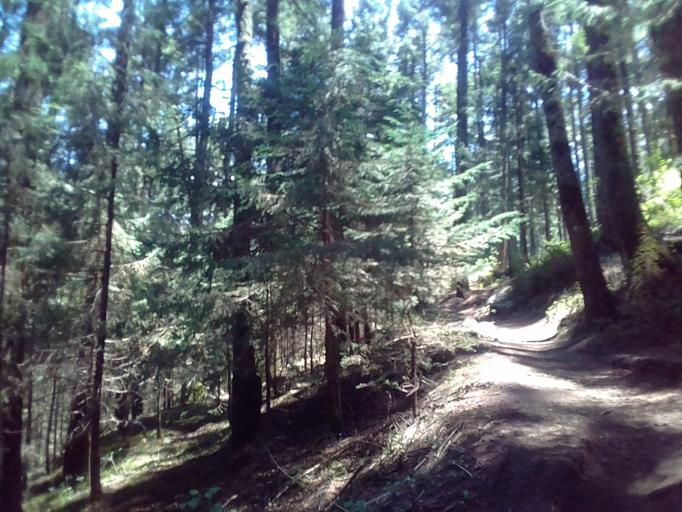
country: MX
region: Mexico City
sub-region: Cuajimalpa de Morelos
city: San Lorenzo Acopilco
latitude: 19.2906
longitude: -99.3348
